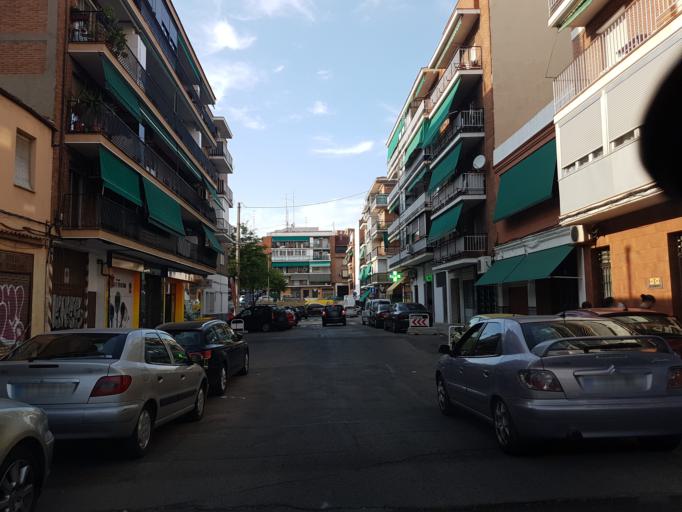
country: ES
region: Madrid
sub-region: Provincia de Madrid
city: Moratalaz
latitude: 40.4293
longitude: -3.6468
